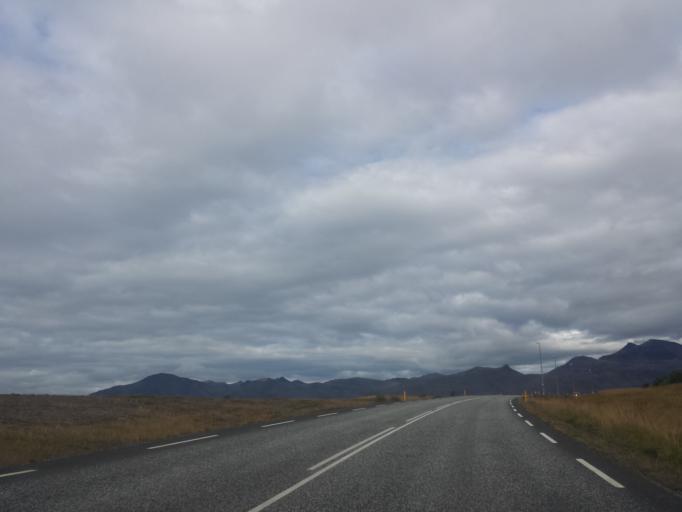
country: IS
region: West
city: Borgarnes
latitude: 64.3807
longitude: -21.8516
